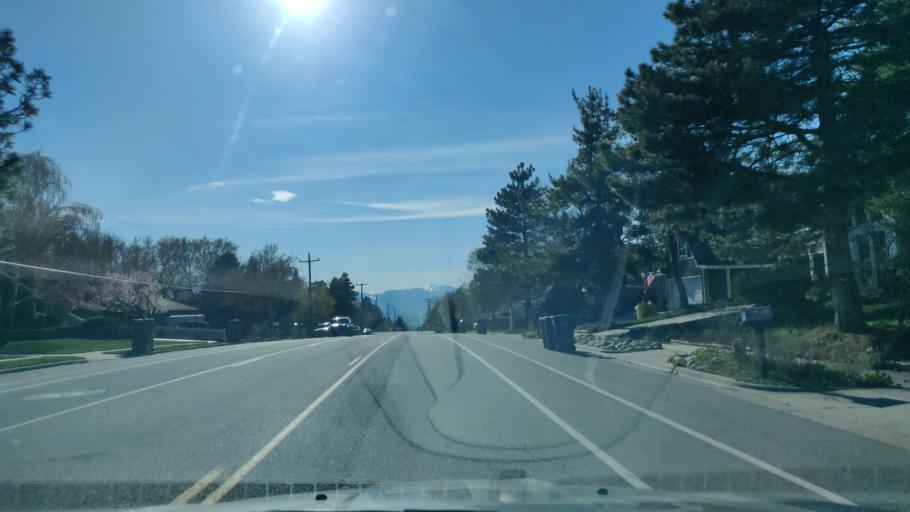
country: US
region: Utah
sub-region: Salt Lake County
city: Cottonwood Heights
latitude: 40.6095
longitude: -111.7934
